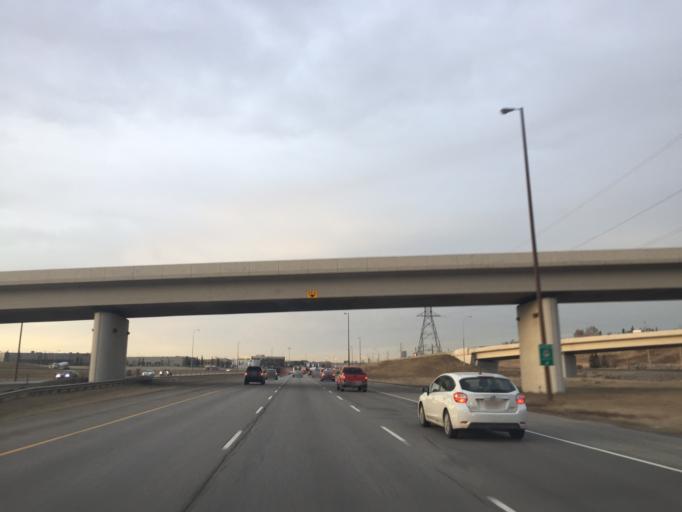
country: CA
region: Alberta
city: Calgary
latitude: 51.1264
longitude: -114.0462
